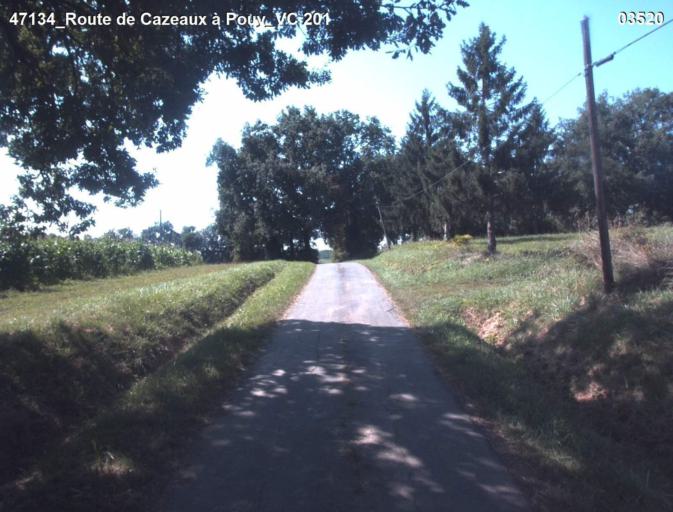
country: FR
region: Aquitaine
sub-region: Departement du Lot-et-Garonne
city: Mezin
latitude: 44.0293
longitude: 0.3070
